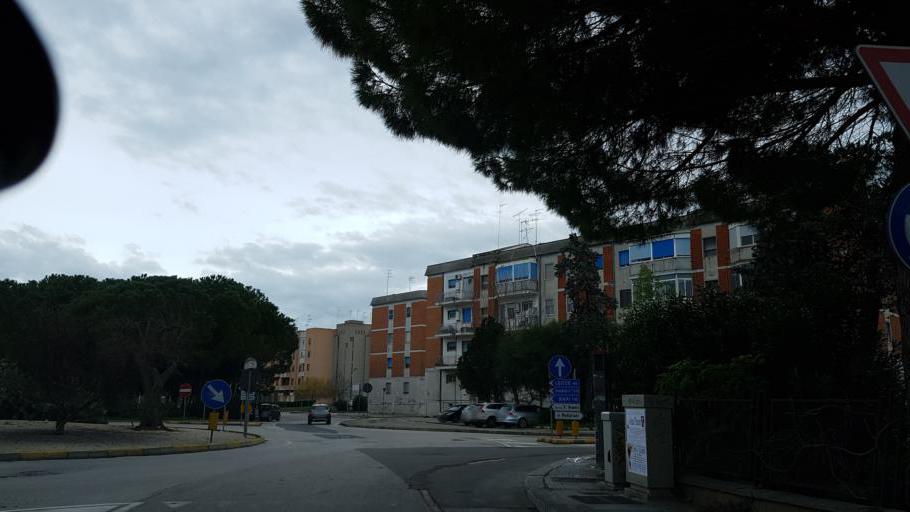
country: IT
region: Apulia
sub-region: Provincia di Brindisi
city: Brindisi
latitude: 40.6215
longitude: 17.9252
